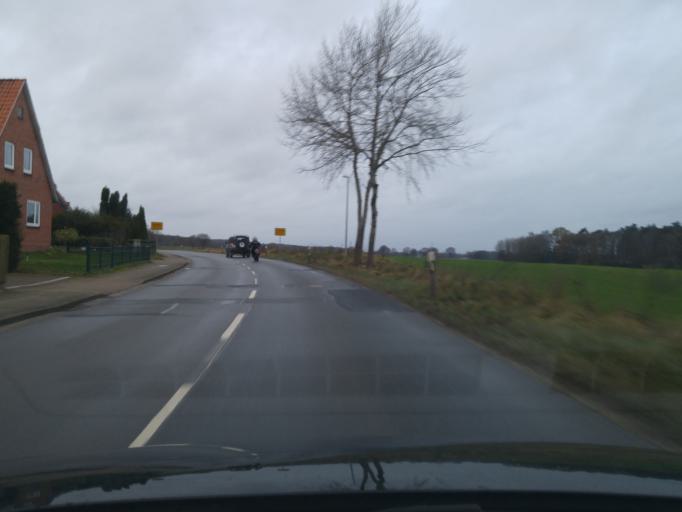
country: DE
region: Lower Saxony
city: Rullstorf
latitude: 53.2701
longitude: 10.5170
